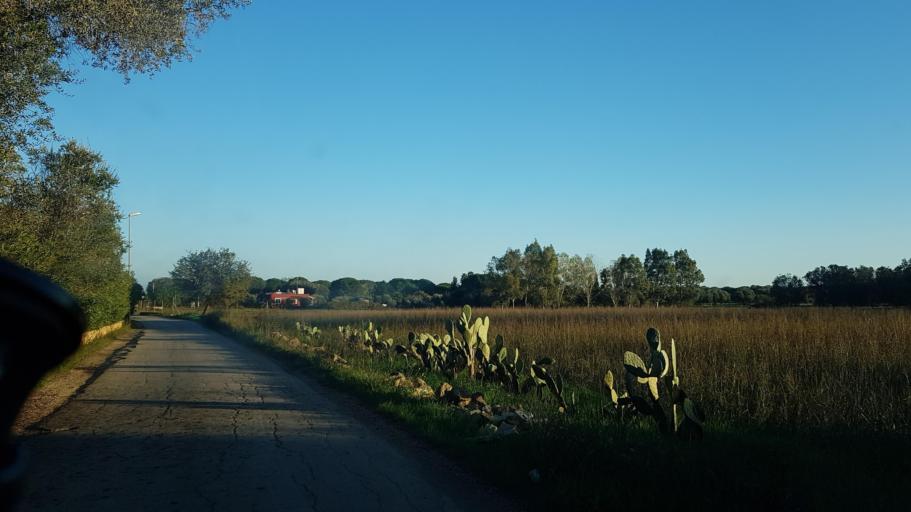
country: IT
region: Apulia
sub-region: Provincia di Brindisi
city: Mesagne
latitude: 40.5640
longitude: 17.7790
